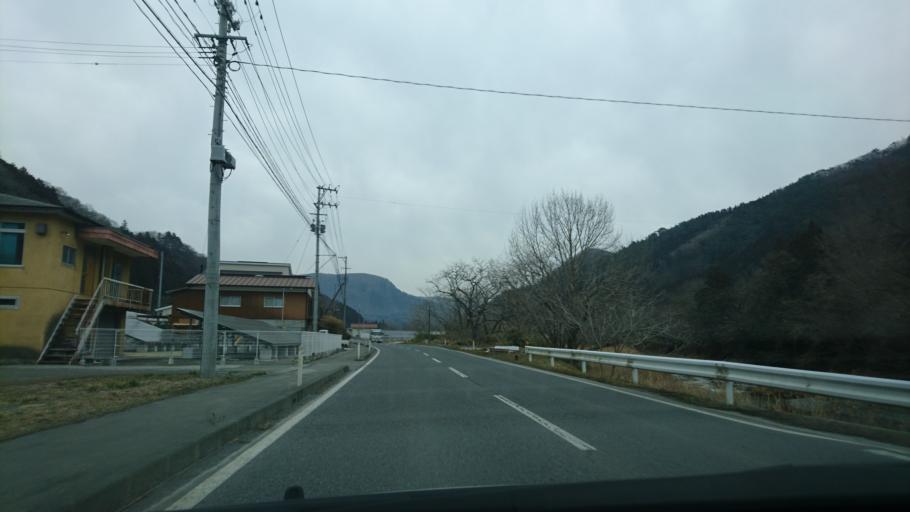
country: JP
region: Iwate
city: Tono
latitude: 39.1783
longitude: 141.5469
